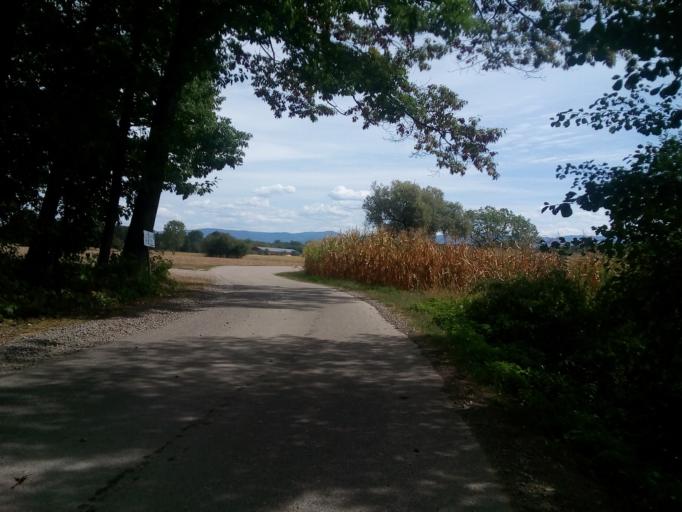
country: DE
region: Baden-Wuerttemberg
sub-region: Karlsruhe Region
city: Lichtenau
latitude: 48.7010
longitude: 8.0183
